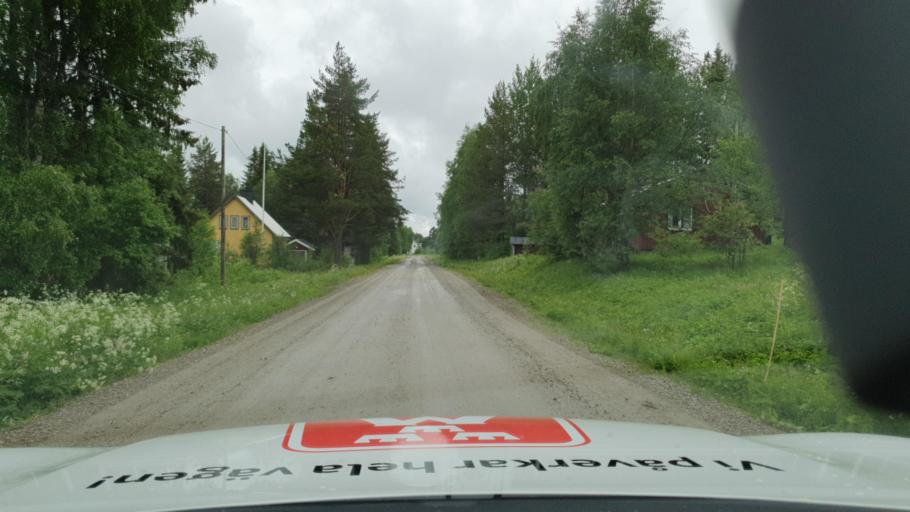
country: SE
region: Vaesterbotten
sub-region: Dorotea Kommun
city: Dorotea
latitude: 64.0147
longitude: 16.7962
